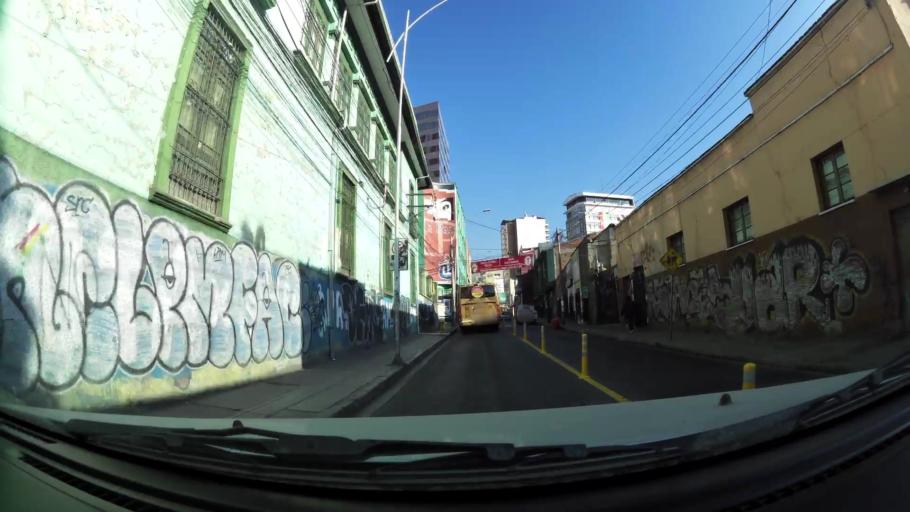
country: BO
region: La Paz
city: La Paz
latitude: -16.5017
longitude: -68.1318
